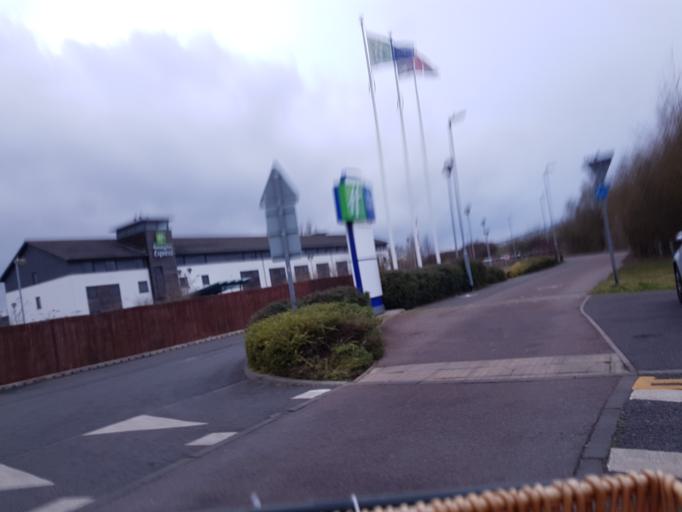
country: GB
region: England
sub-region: Cambridgeshire
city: Cambridge
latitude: 52.1946
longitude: 0.1661
